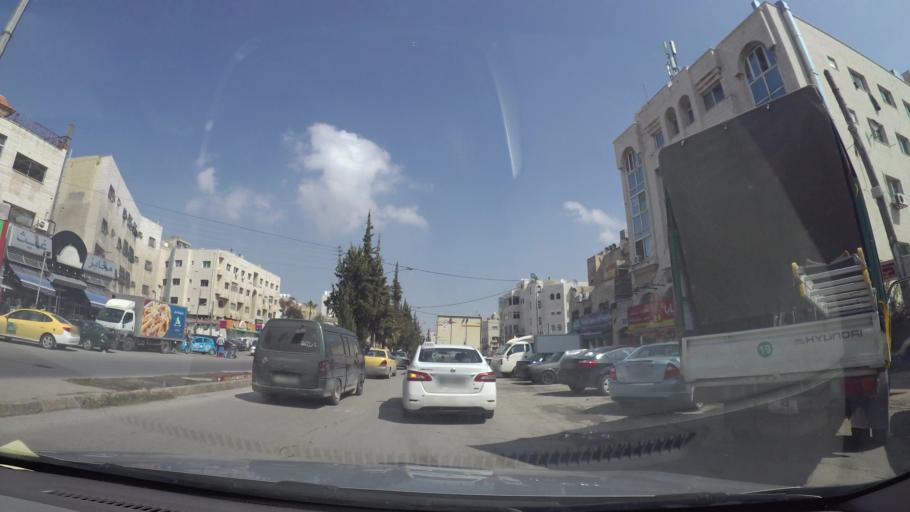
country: JO
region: Amman
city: Al Bunayyat ash Shamaliyah
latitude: 31.9250
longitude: 35.9036
